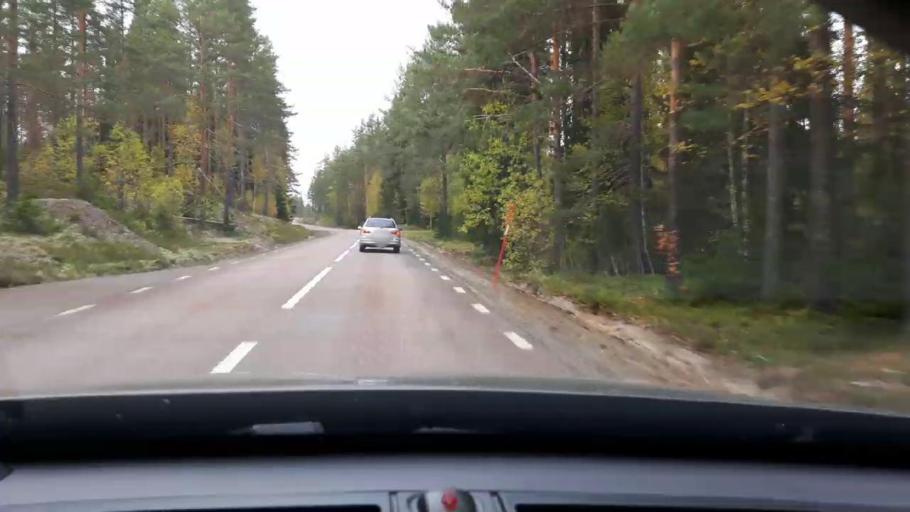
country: SE
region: Dalarna
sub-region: Gagnefs Kommun
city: Mockfjard
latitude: 60.3567
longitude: 14.8421
